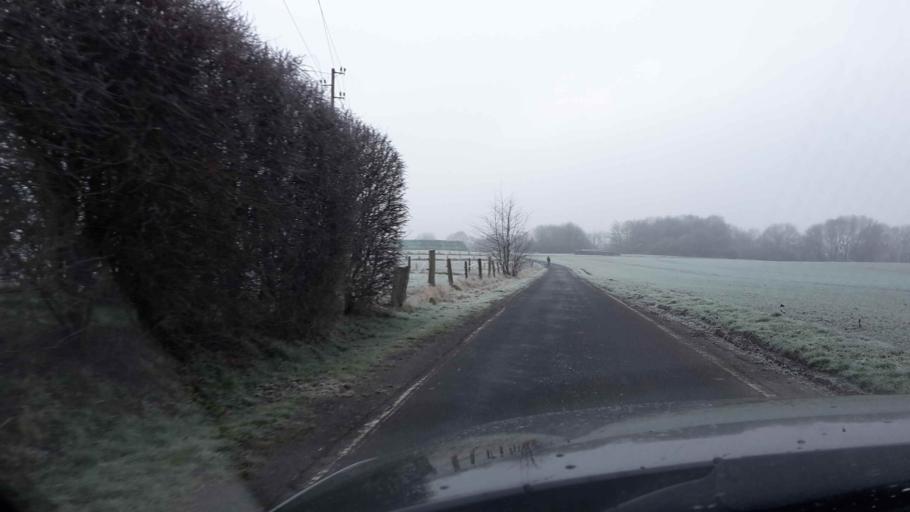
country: DE
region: North Rhine-Westphalia
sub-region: Regierungsbezirk Koln
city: Hennef
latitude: 50.7288
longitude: 7.2929
